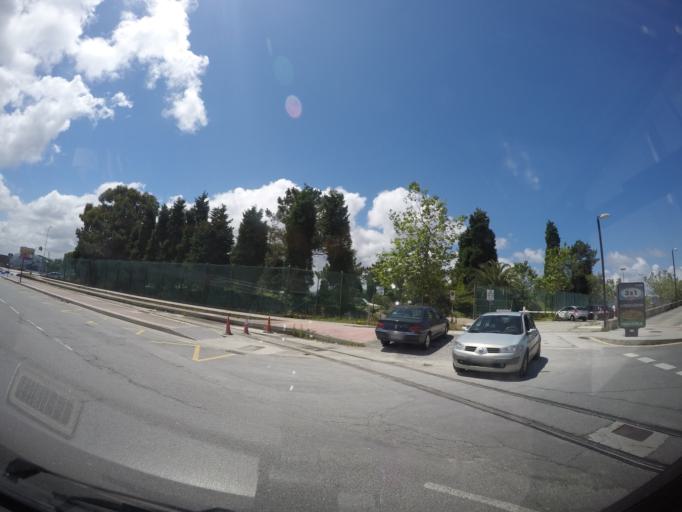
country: ES
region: Galicia
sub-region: Provincia da Coruna
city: A Coruna
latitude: 43.3679
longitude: -8.3919
